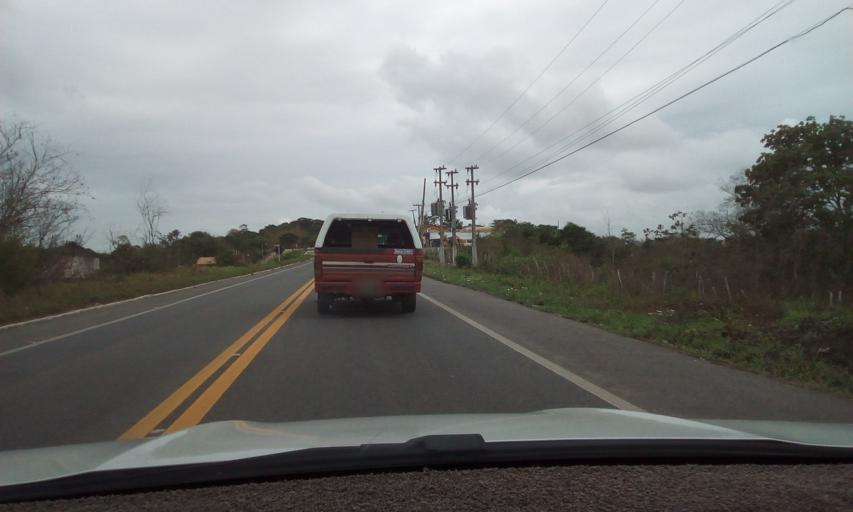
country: BR
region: Paraiba
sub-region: Lagoa Seca
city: Lagoa Seca
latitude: -7.1736
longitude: -35.8598
